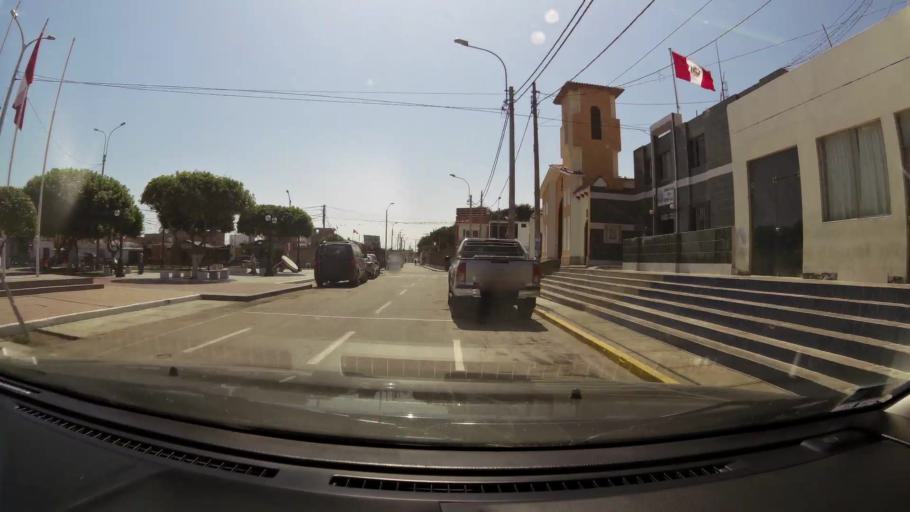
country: PE
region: Lima
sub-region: Provincia de Canete
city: San Vicente de Canete
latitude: -13.0250
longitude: -76.4789
